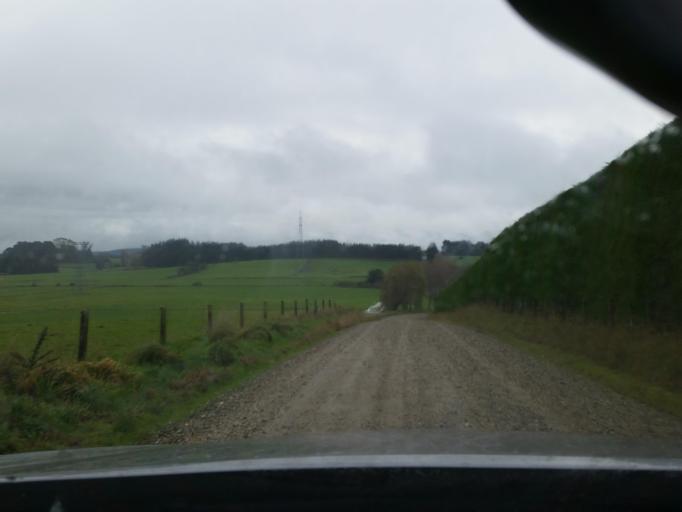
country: NZ
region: Southland
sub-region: Invercargill City
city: Invercargill
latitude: -46.3076
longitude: 168.4789
